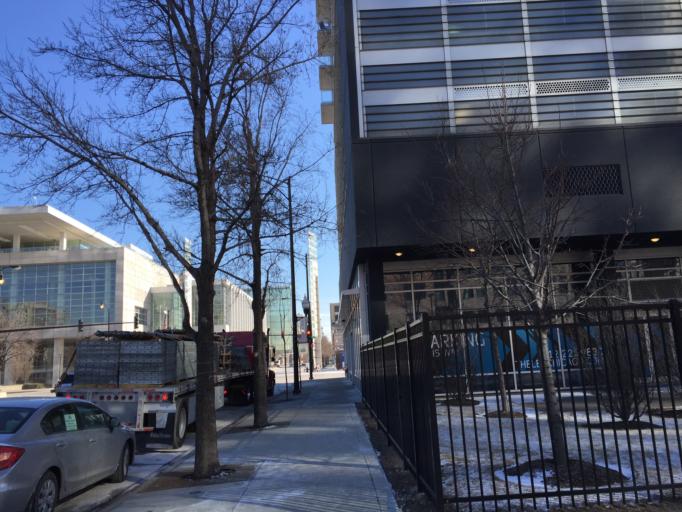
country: US
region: Illinois
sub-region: Cook County
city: Chicago
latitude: 41.8535
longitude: -87.6224
